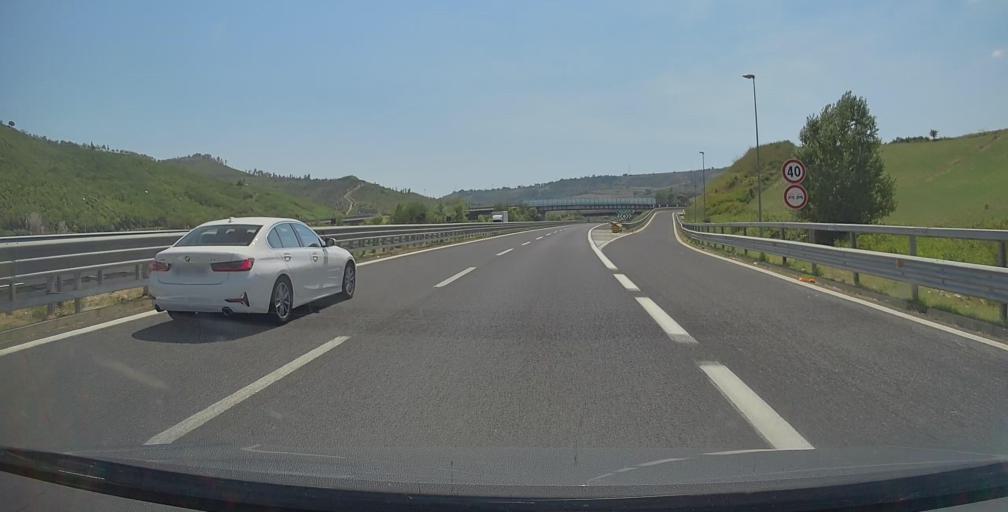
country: IT
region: Calabria
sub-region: Provincia di Vibo-Valentia
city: Paravati
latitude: 38.5662
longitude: 16.0845
